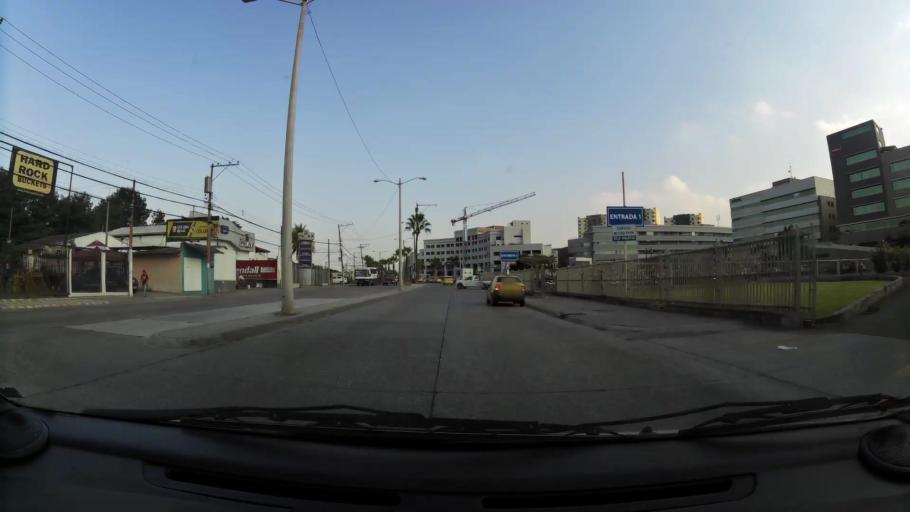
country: EC
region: Guayas
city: Guayaquil
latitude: -2.1499
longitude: -79.9058
